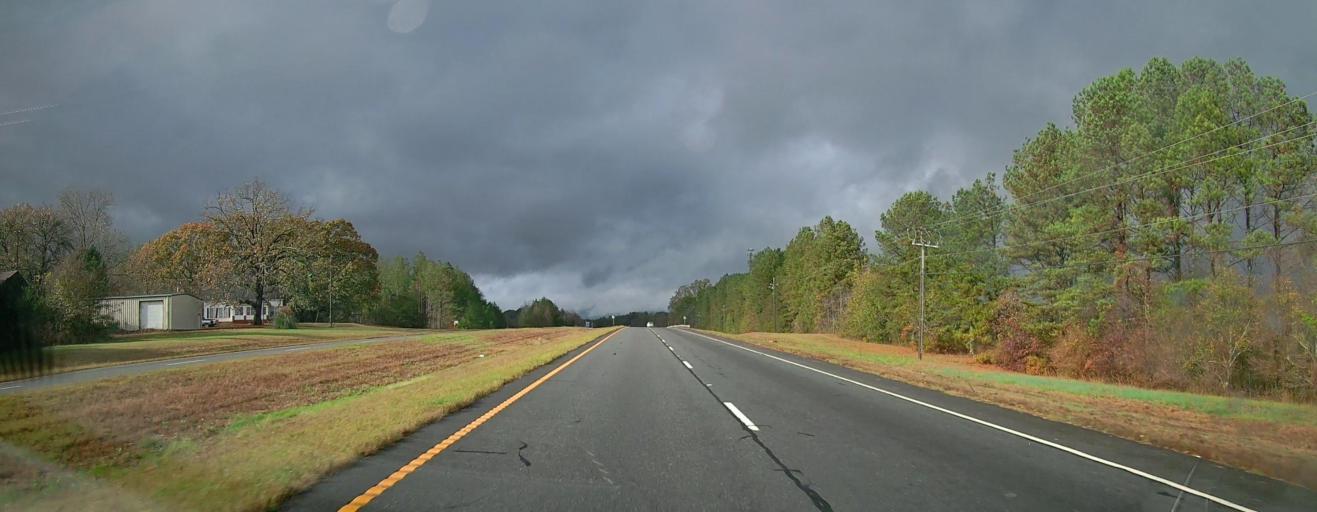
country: US
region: Georgia
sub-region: Clarke County
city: Country Club Estates
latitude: 34.0432
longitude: -83.4039
